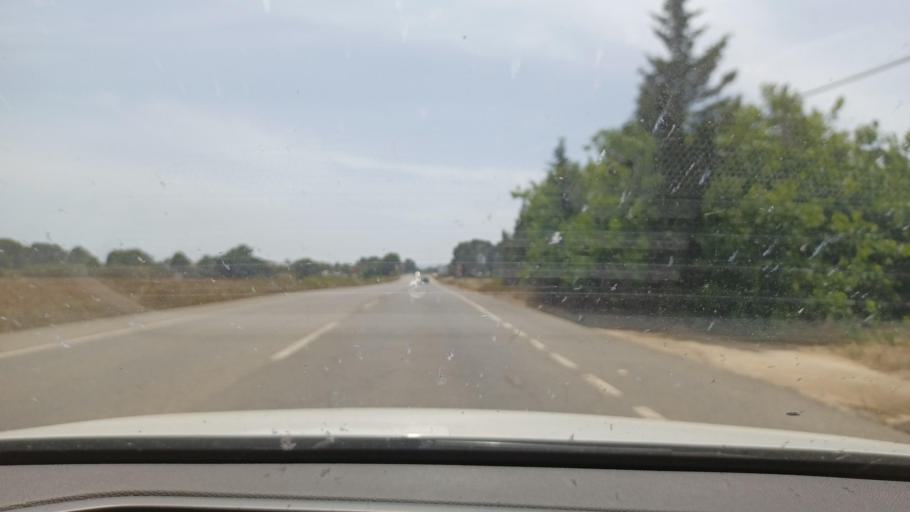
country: ES
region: Catalonia
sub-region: Provincia de Tarragona
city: Cambrils
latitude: 41.0527
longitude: 1.0042
